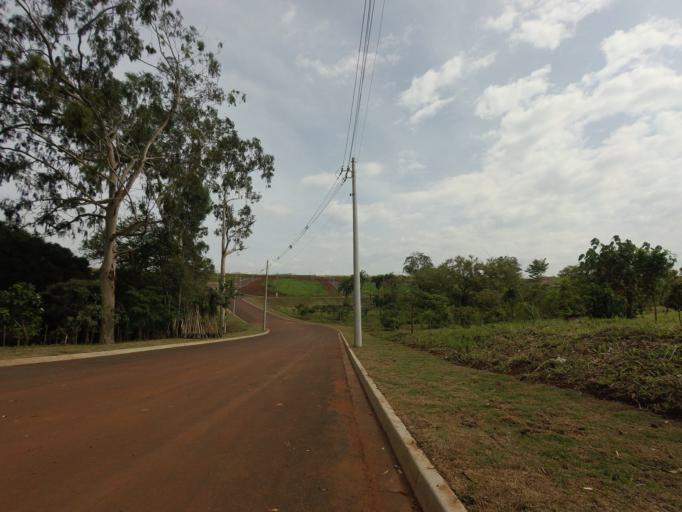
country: BR
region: Sao Paulo
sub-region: Piracicaba
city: Piracicaba
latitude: -22.7657
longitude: -47.5809
